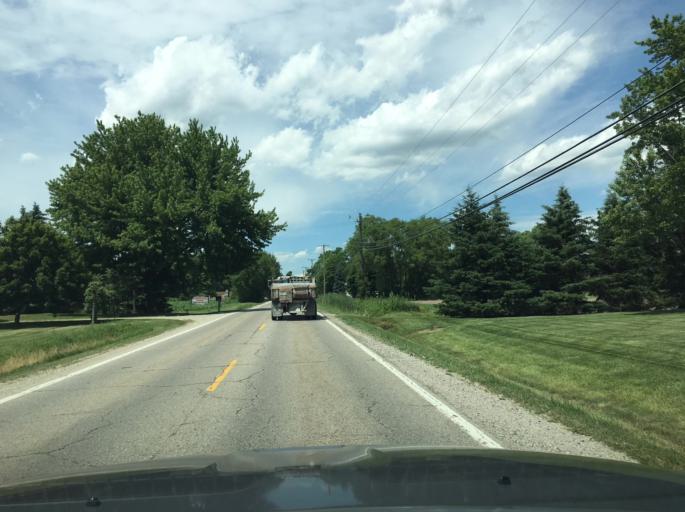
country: US
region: Michigan
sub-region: Macomb County
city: Romeo
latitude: 42.7433
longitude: -82.9604
